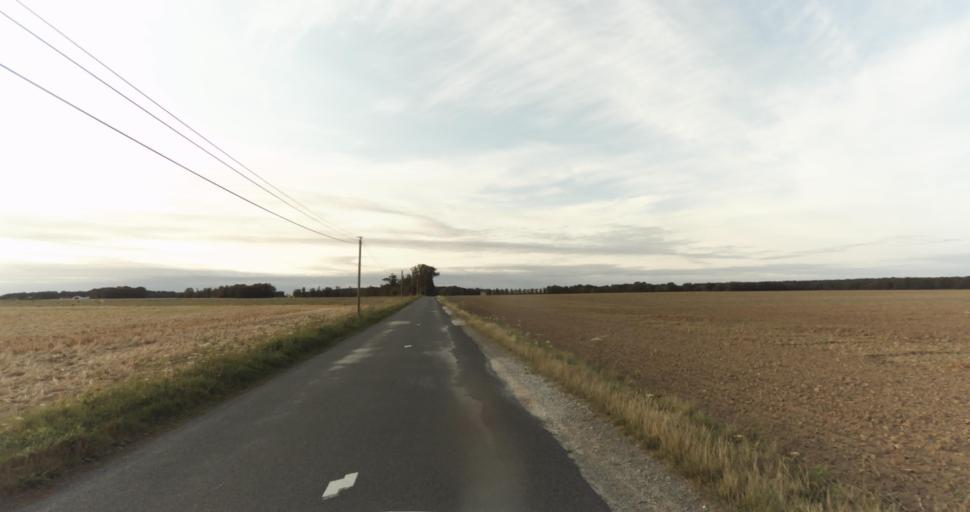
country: FR
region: Haute-Normandie
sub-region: Departement de l'Eure
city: Marcilly-sur-Eure
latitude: 48.8691
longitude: 1.2730
